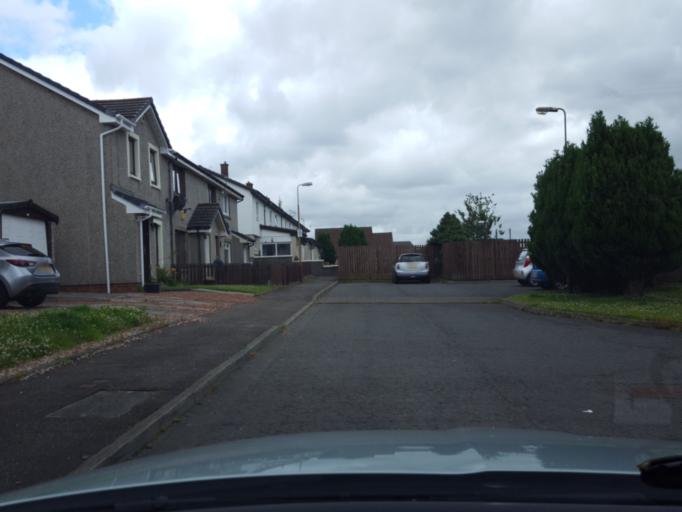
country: GB
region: Scotland
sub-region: West Lothian
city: Blackburn
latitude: 55.8754
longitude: -3.6168
